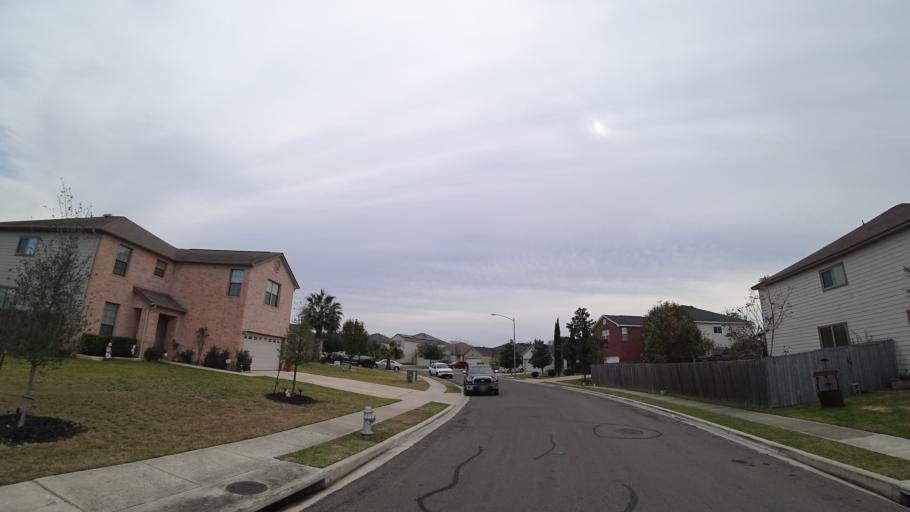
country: US
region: Texas
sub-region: Travis County
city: Onion Creek
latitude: 30.1585
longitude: -97.7439
